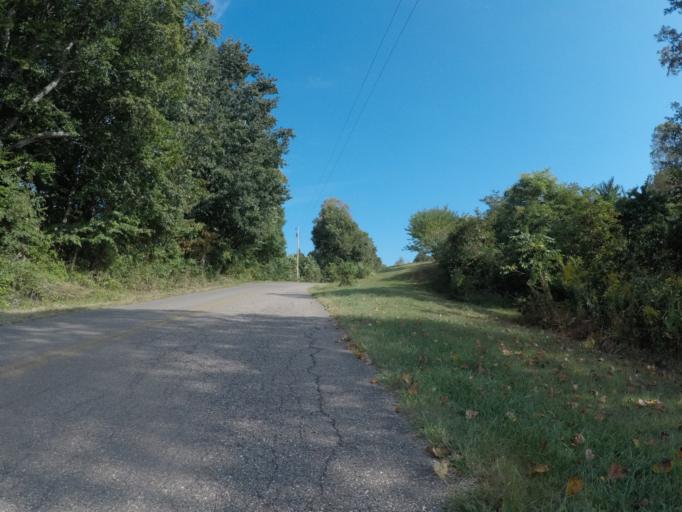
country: US
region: West Virginia
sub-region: Cabell County
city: Lesage
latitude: 38.5987
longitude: -82.4141
